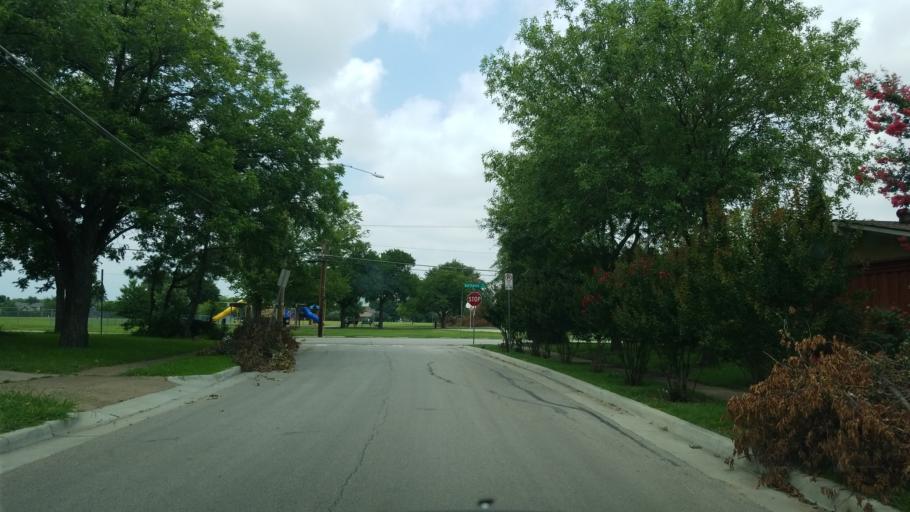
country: US
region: Texas
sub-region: Dallas County
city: Farmers Branch
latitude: 32.9035
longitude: -96.8778
